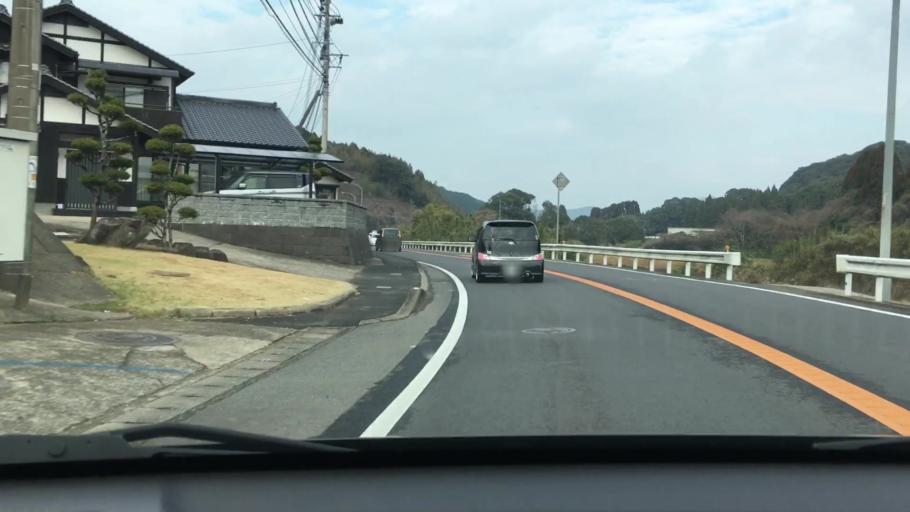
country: JP
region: Saga Prefecture
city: Imaricho-ko
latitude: 33.3182
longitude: 129.9291
